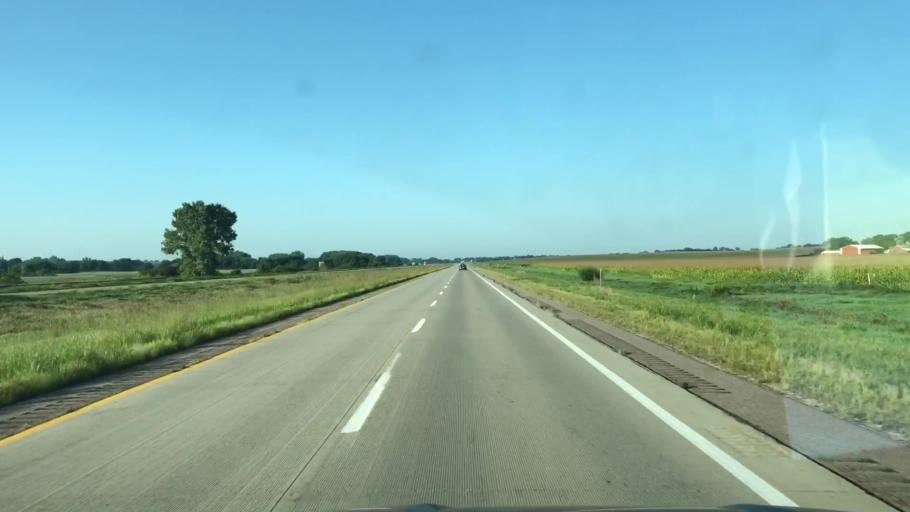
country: US
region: Iowa
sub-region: Plymouth County
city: Le Mars
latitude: 42.8795
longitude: -96.1024
